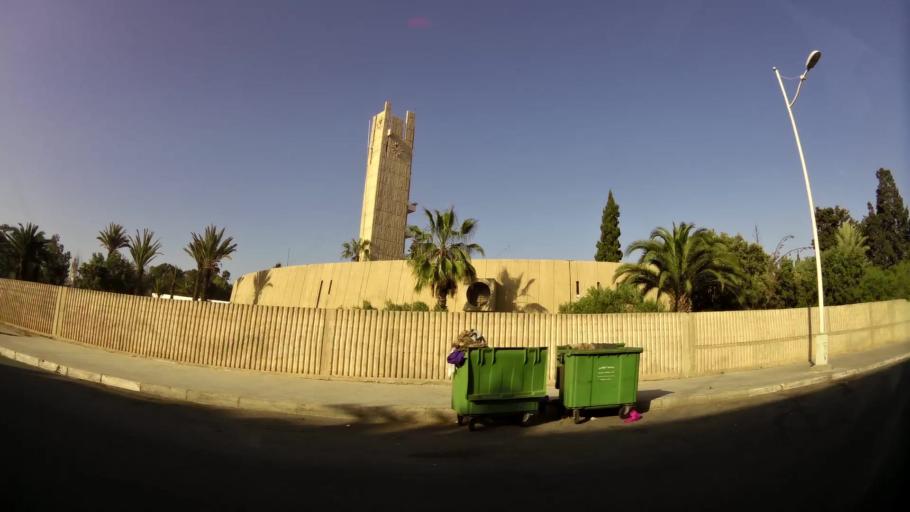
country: MA
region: Souss-Massa-Draa
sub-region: Agadir-Ida-ou-Tnan
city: Agadir
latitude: 30.4172
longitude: -9.5926
